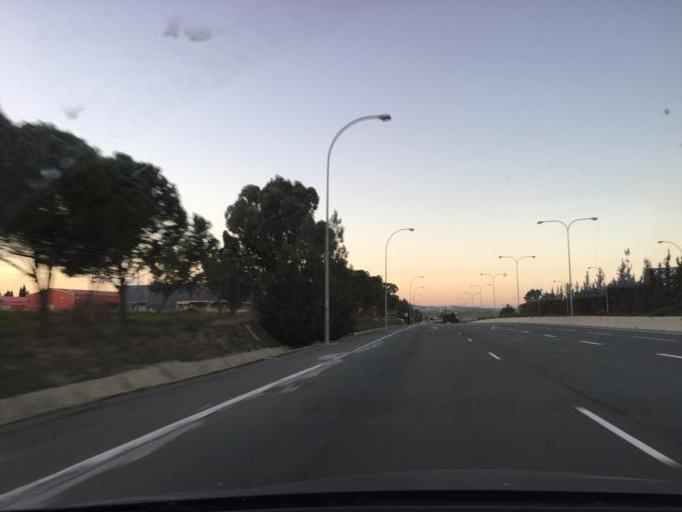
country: CY
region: Larnaka
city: Dhromolaxia
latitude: 34.9037
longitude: 33.5703
